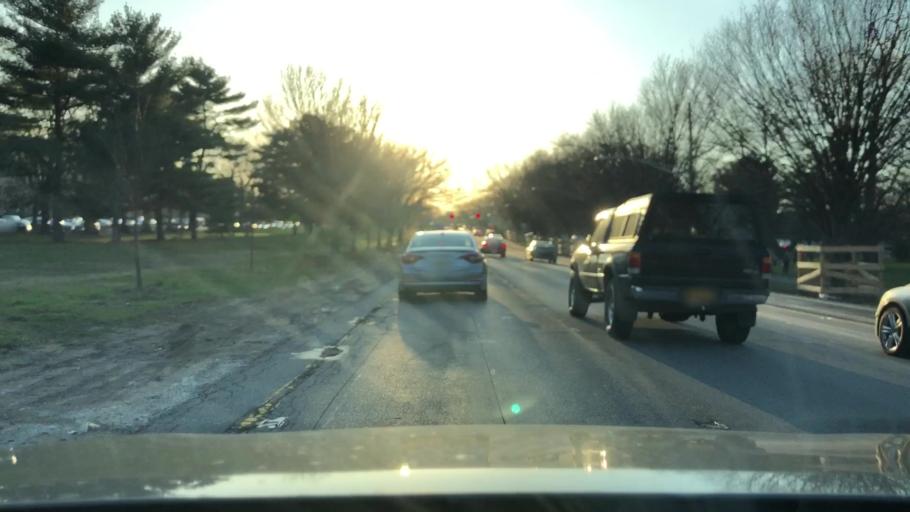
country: US
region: New York
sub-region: Bronx
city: The Bronx
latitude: 40.8573
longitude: -73.8409
